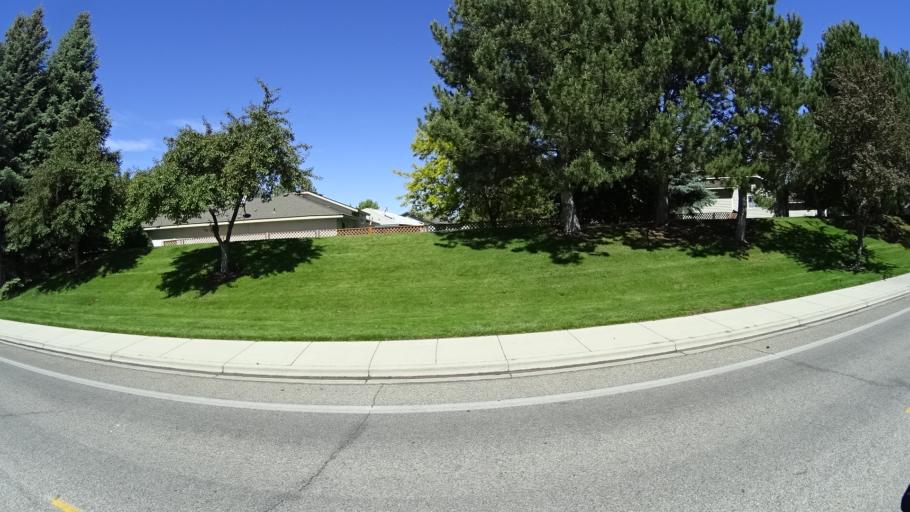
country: US
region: Idaho
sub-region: Ada County
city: Boise
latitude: 43.5518
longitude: -116.1375
